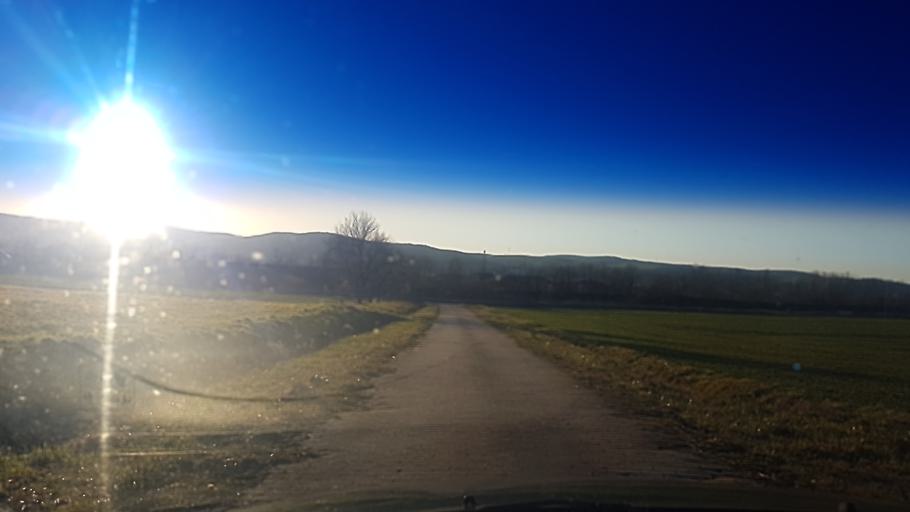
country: DE
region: Bavaria
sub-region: Upper Franconia
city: Lauter
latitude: 49.9483
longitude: 10.7614
